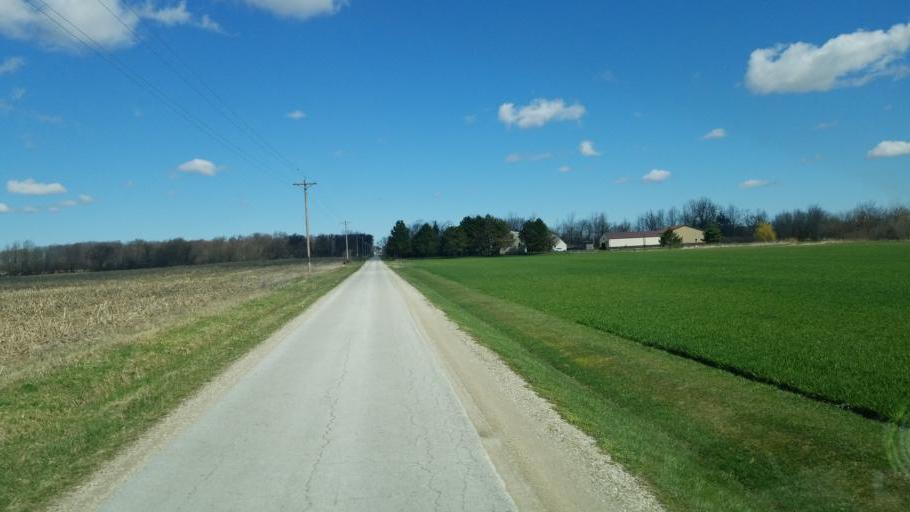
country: US
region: Ohio
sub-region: Sandusky County
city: Mount Carmel
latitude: 41.2279
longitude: -82.9370
